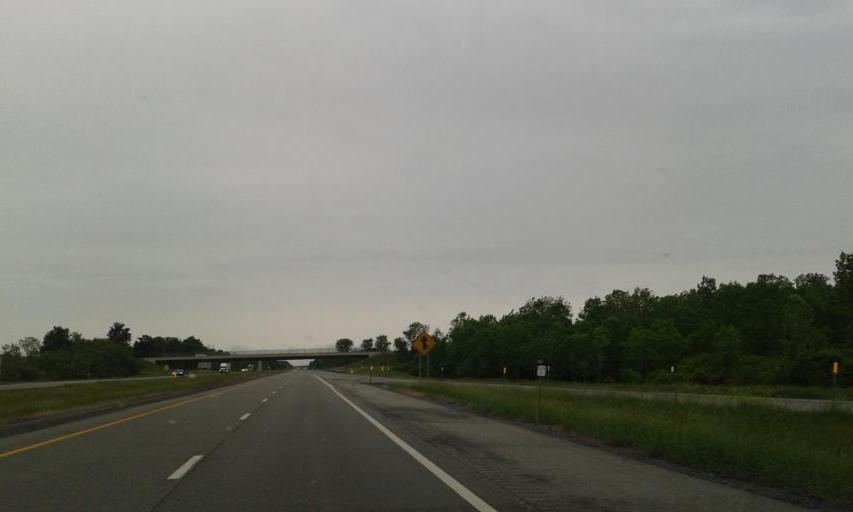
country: US
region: New York
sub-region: Genesee County
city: Le Roy
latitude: 43.0291
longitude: -77.9664
